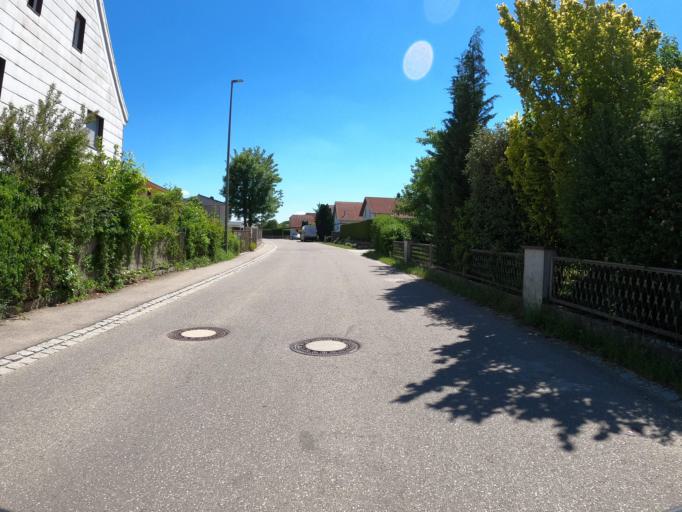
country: DE
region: Bavaria
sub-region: Swabia
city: Pfaffenhofen an der Roth
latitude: 48.3480
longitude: 10.1536
